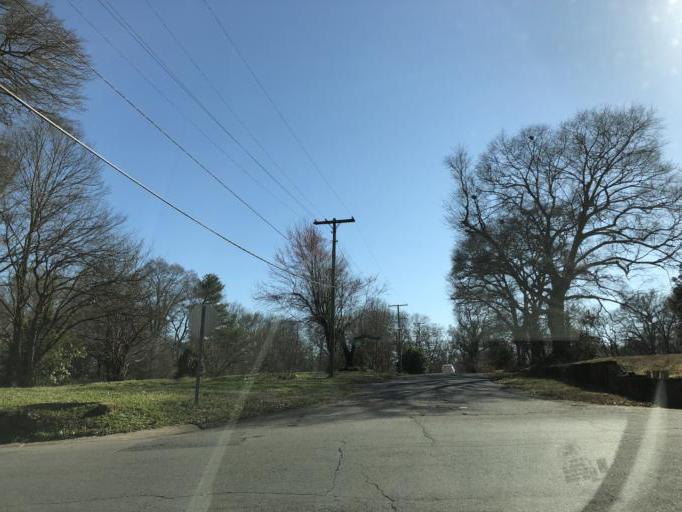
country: US
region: North Carolina
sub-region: Cleveland County
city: Shelby
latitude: 35.2768
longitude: -81.5408
